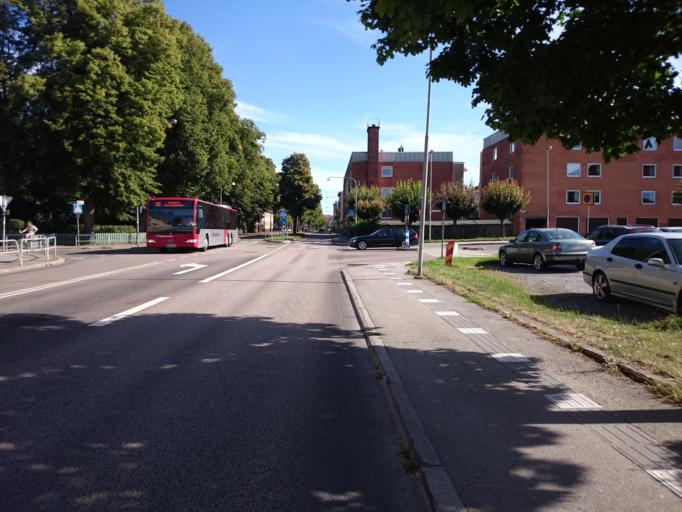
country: SE
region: Blekinge
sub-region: Karlshamns Kommun
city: Karlshamn
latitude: 56.1731
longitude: 14.8668
